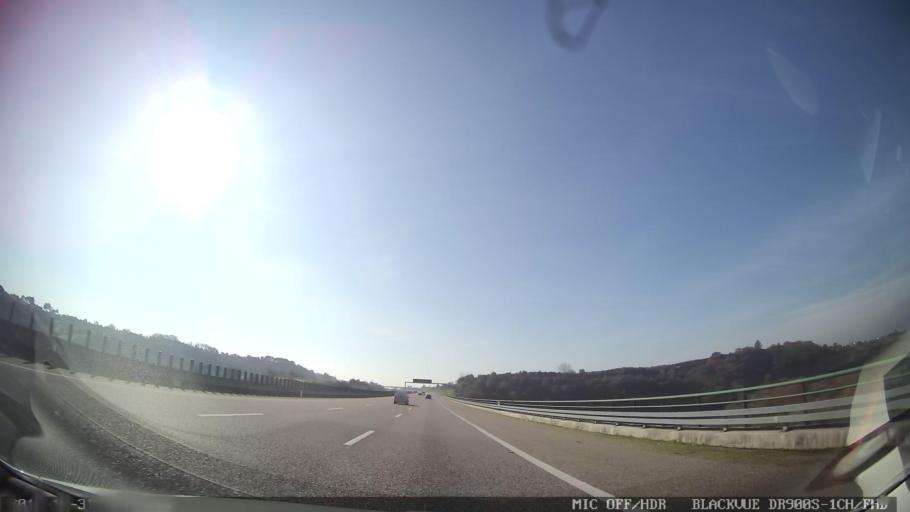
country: PT
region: Santarem
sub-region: Alcanena
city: Alcanena
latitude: 39.3533
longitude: -8.6435
